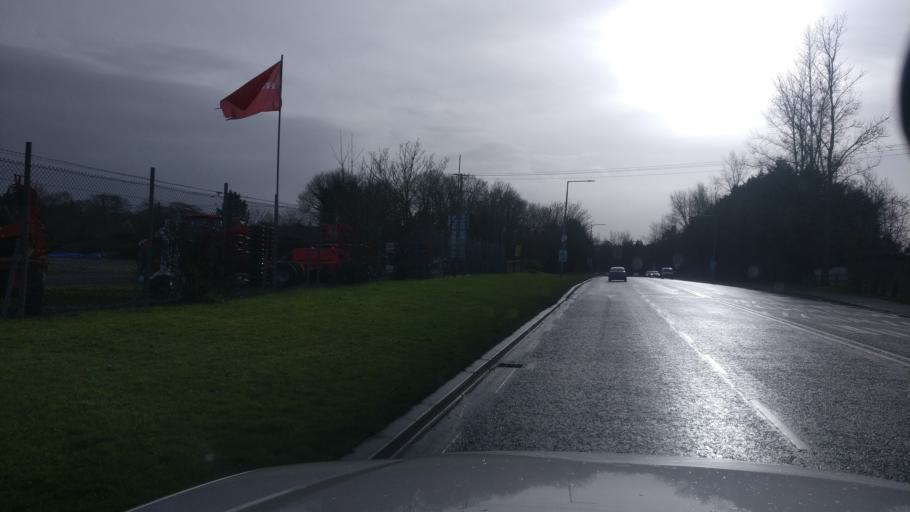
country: IE
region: Leinster
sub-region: Kilkenny
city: Kilkenny
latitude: 52.6491
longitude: -7.2288
